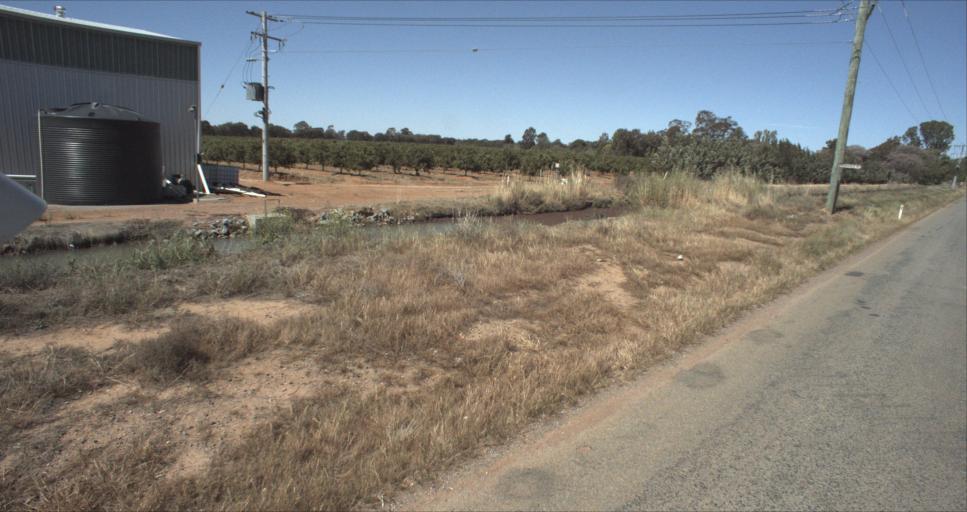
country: AU
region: New South Wales
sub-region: Leeton
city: Leeton
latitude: -34.5468
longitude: 146.3694
